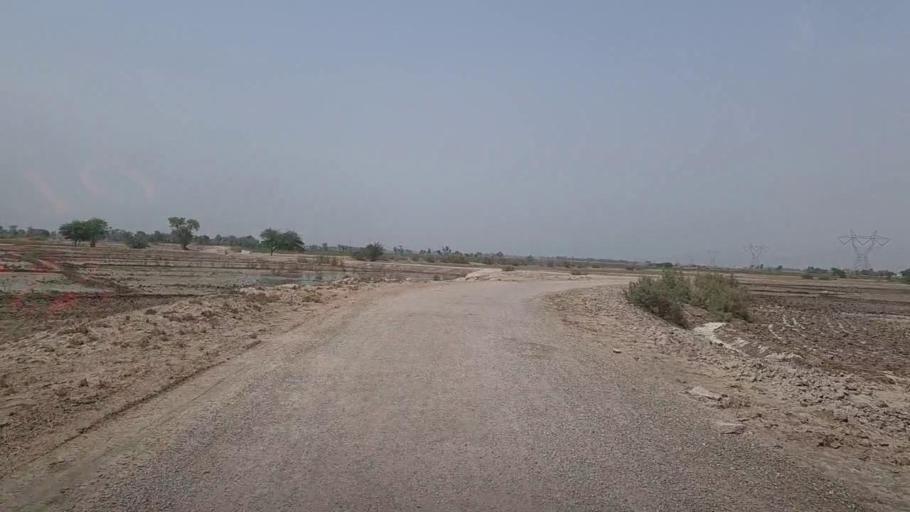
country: PK
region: Sindh
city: Sita Road
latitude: 27.0897
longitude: 67.8560
